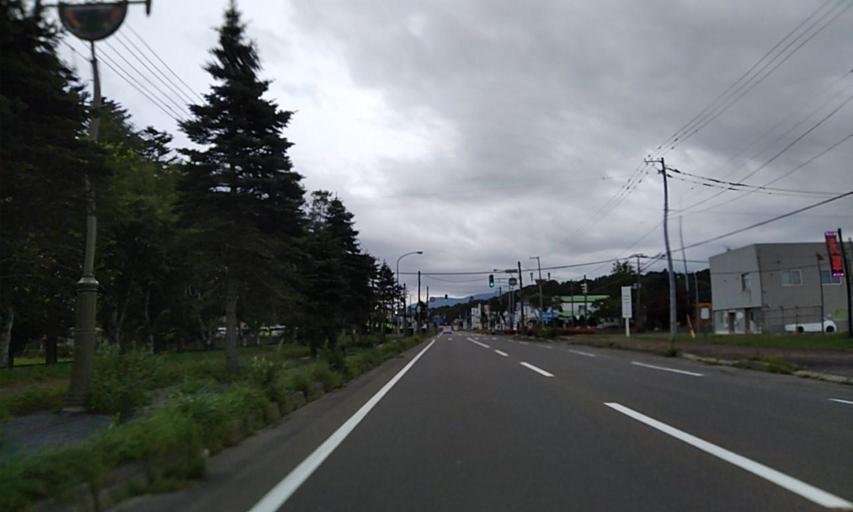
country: JP
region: Hokkaido
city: Obihiro
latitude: 42.2968
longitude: 143.3138
